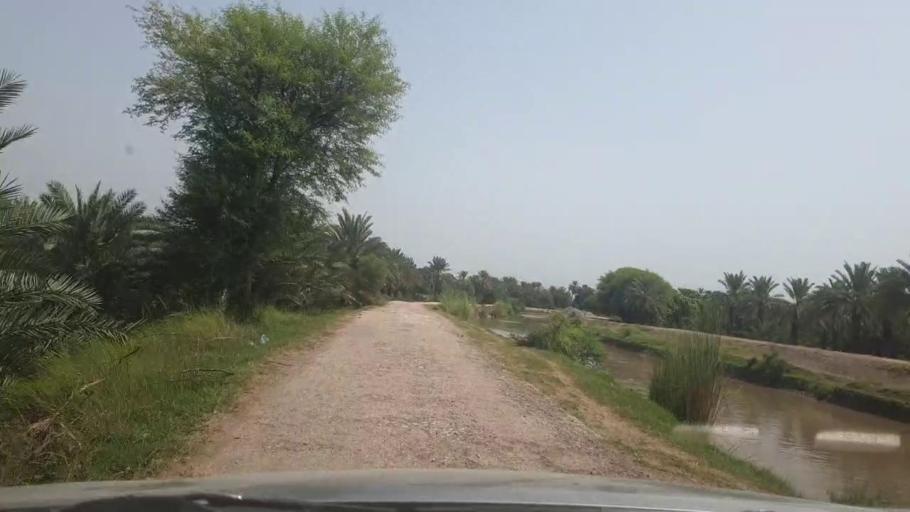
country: PK
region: Sindh
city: Pano Aqil
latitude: 27.8885
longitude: 69.1319
